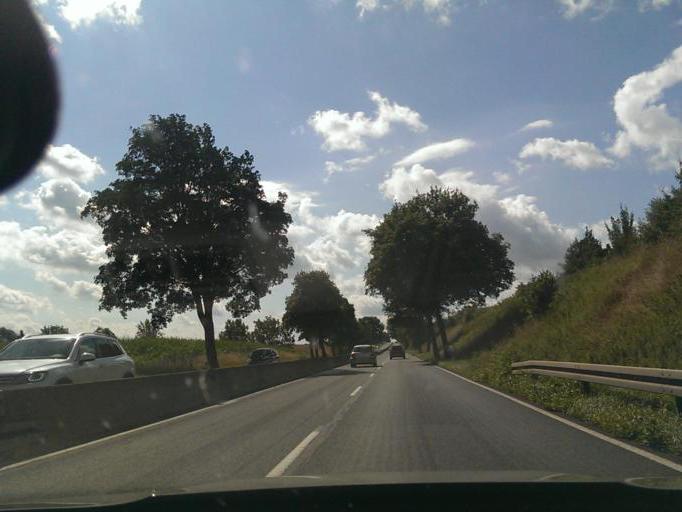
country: DE
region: Lower Saxony
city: Laatzen
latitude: 52.2911
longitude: 9.8334
